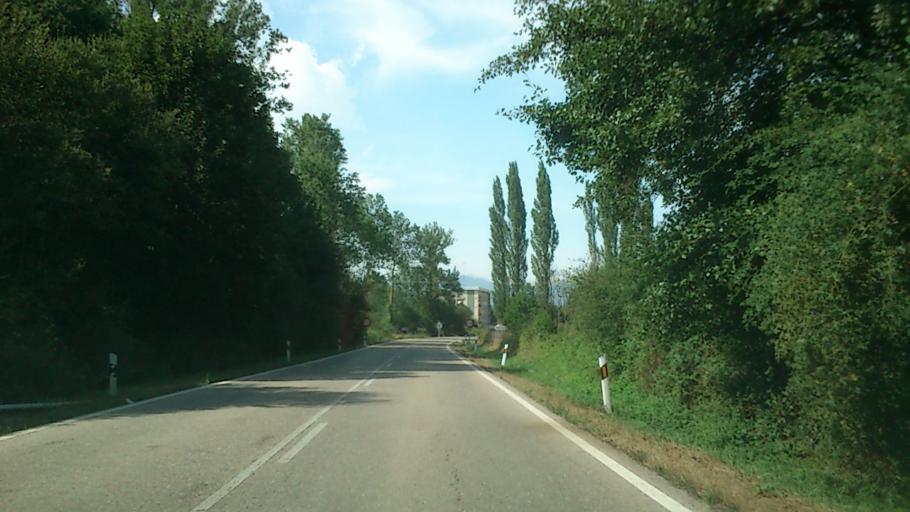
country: ES
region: Castille and Leon
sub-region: Provincia de Burgos
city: Espinosa de los Monteros
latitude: 43.0218
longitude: -3.4836
